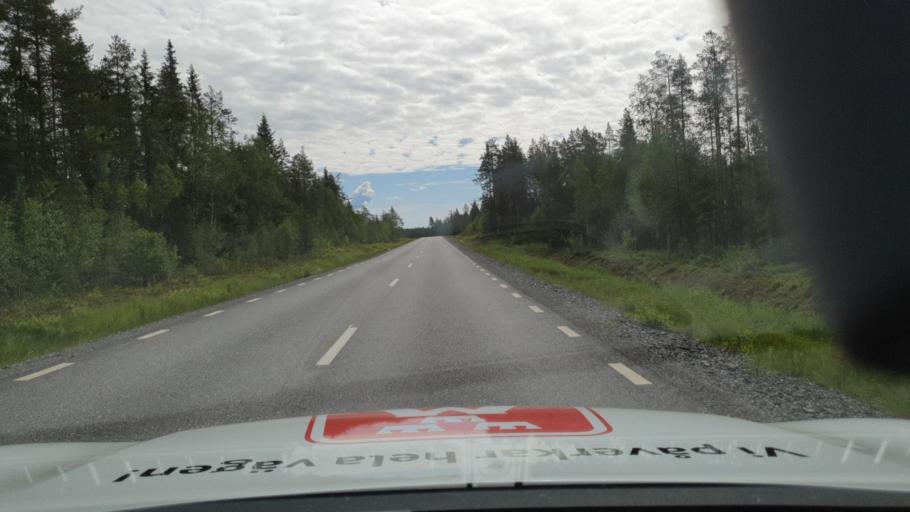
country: SE
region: Vaesterbotten
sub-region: Vindelns Kommun
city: Vindeln
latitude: 64.2501
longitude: 20.0486
